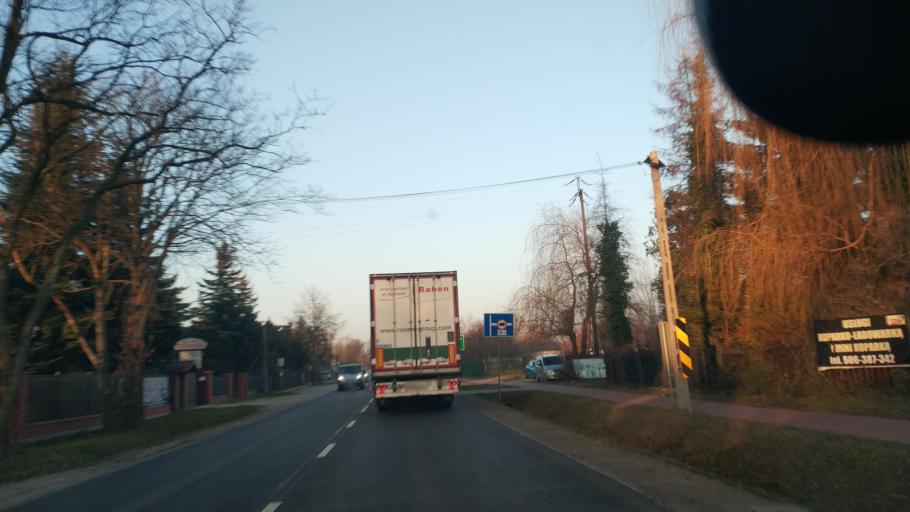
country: PL
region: Masovian Voivodeship
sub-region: Powiat grodziski
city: Milanowek
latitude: 52.0878
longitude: 20.6808
